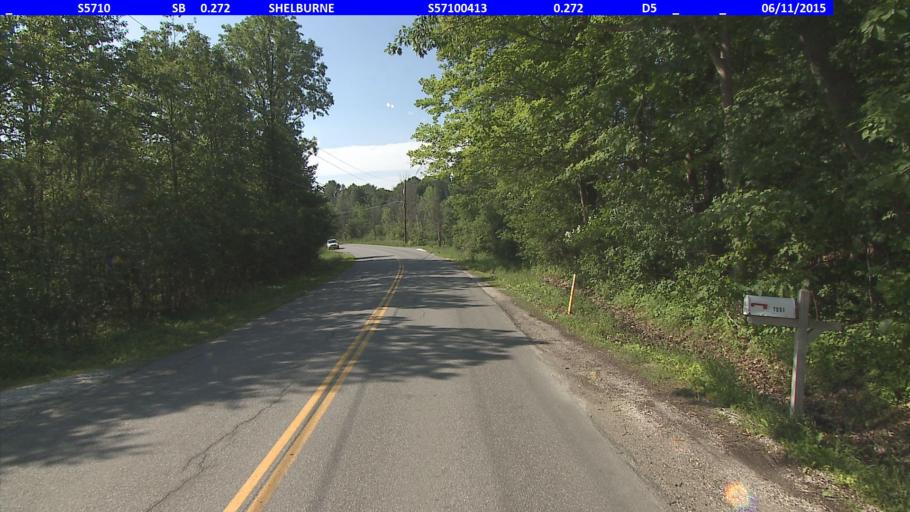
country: US
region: Vermont
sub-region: Chittenden County
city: Hinesburg
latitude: 44.3687
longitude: -73.1808
